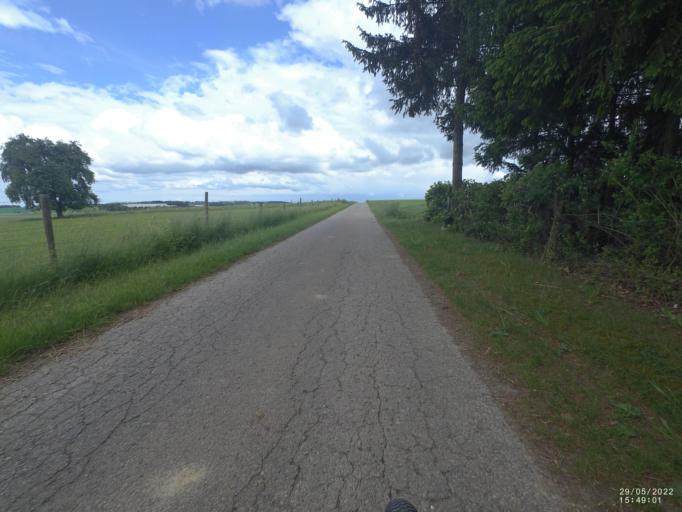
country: DE
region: Baden-Wuerttemberg
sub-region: Tuebingen Region
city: Ballendorf
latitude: 48.5847
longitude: 10.1094
